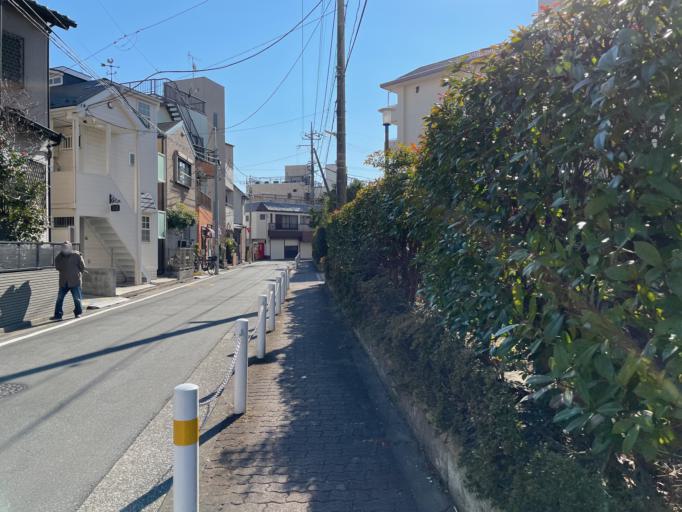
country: JP
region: Saitama
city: Soka
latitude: 35.7939
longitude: 139.7870
